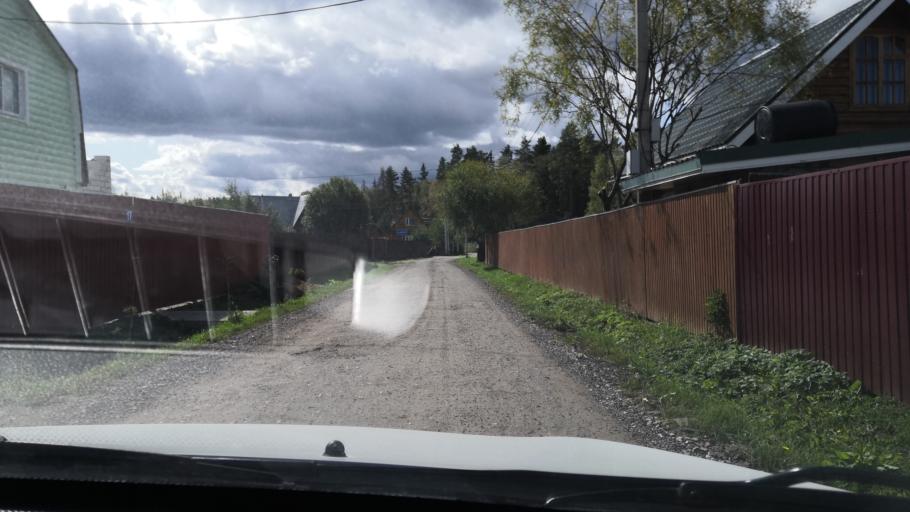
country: RU
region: Moskovskaya
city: Povarovo
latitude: 56.0598
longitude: 37.0223
